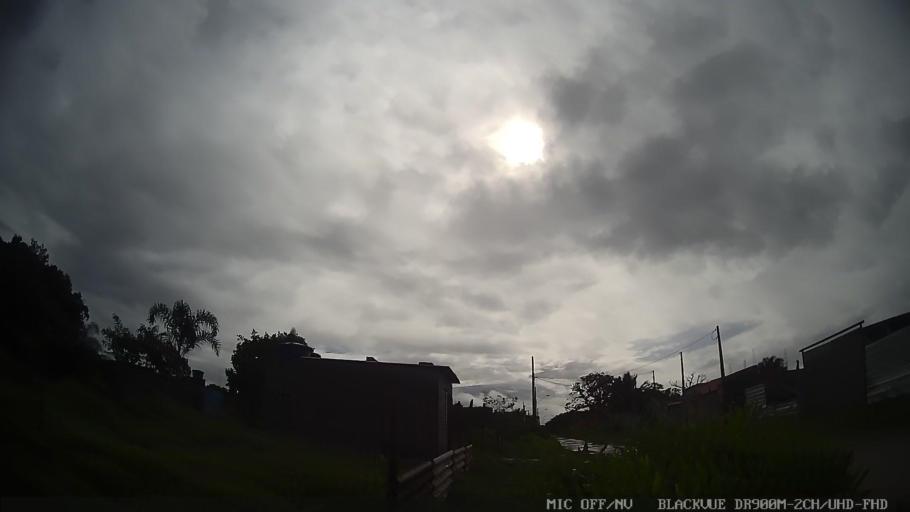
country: BR
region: Sao Paulo
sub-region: Itanhaem
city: Itanhaem
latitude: -24.2322
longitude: -46.8957
